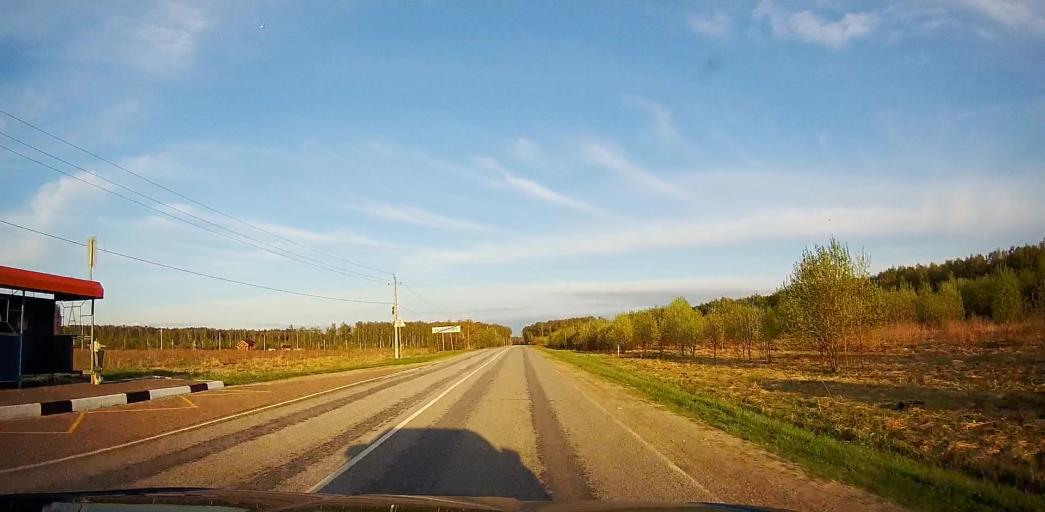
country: RU
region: Moskovskaya
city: Meshcherino
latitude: 55.2303
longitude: 38.3761
